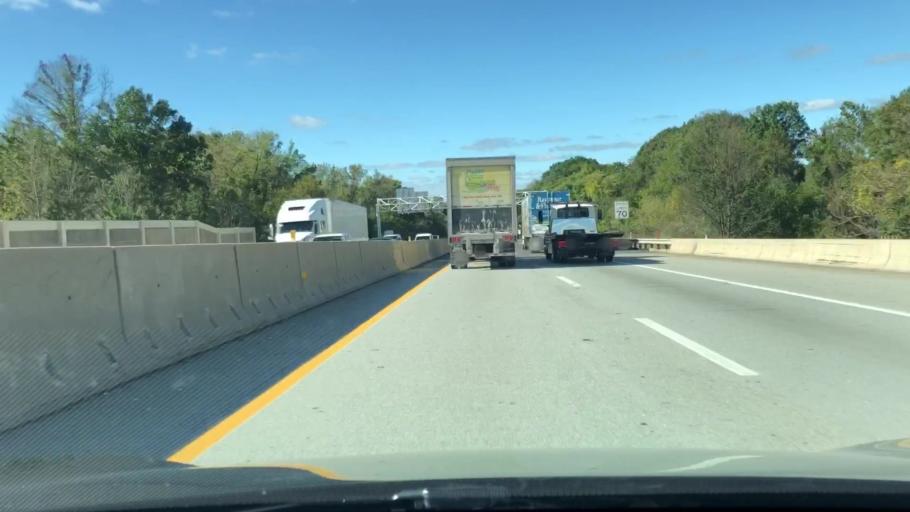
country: US
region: Pennsylvania
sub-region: Montgomery County
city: King of Prussia
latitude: 40.0902
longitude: -75.4150
